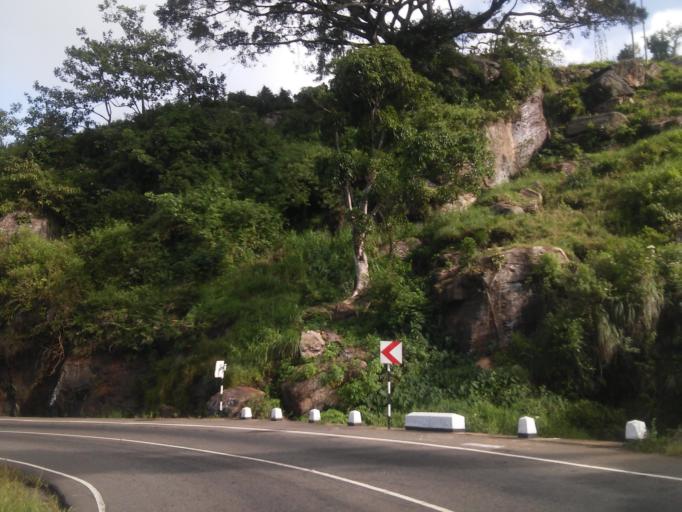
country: LK
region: Uva
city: Haputale
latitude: 6.7595
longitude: 80.9426
